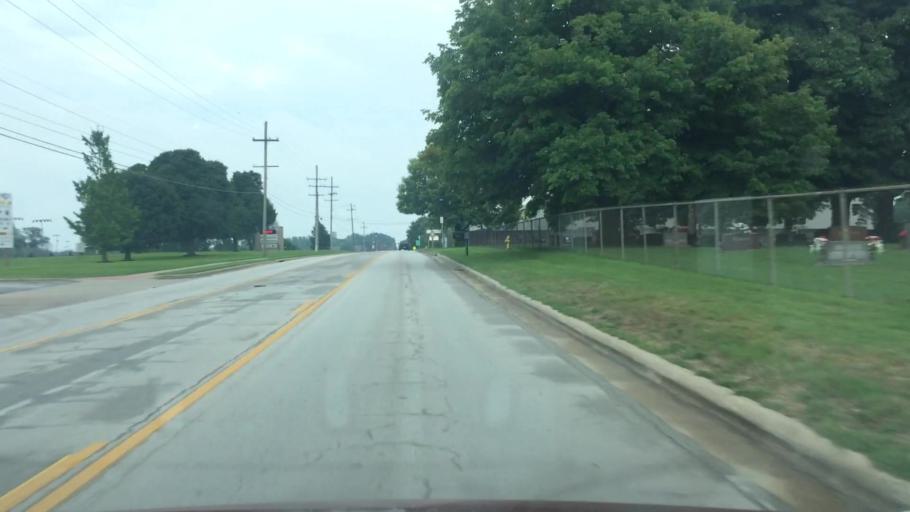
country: US
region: Missouri
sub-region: Greene County
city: Springfield
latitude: 37.2179
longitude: -93.2513
